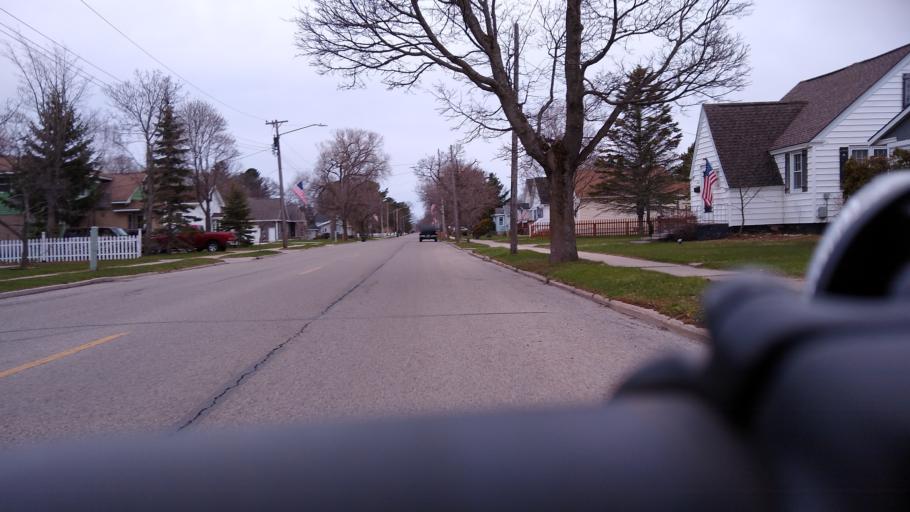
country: US
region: Michigan
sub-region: Delta County
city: Escanaba
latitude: 45.7309
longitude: -87.0640
